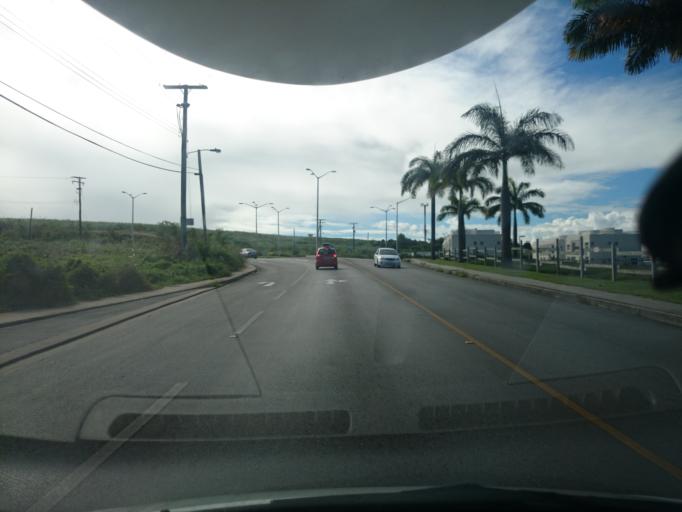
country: BB
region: Christ Church
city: Oistins
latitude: 13.1082
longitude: -59.5412
